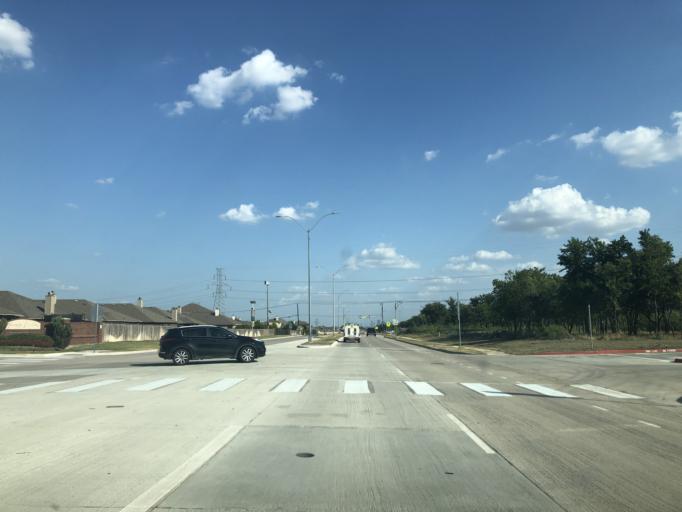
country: US
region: Texas
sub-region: Tarrant County
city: Saginaw
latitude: 32.8422
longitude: -97.3883
